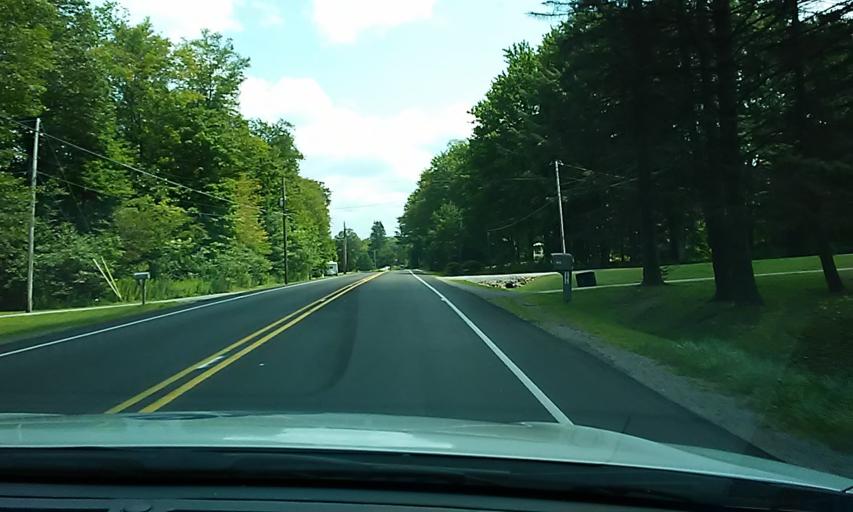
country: US
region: Pennsylvania
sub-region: Elk County
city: Saint Marys
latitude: 41.4437
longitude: -78.4924
